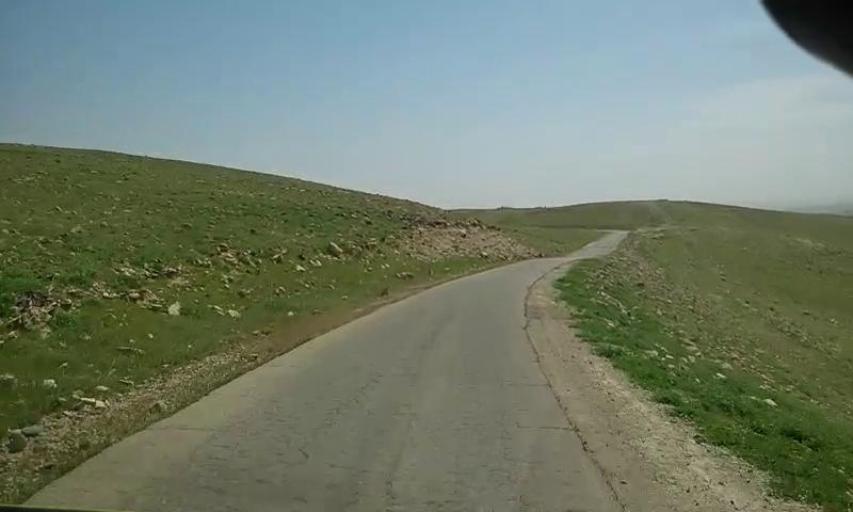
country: PS
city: `Arab ar Rashaydah
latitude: 31.5444
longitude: 35.2586
